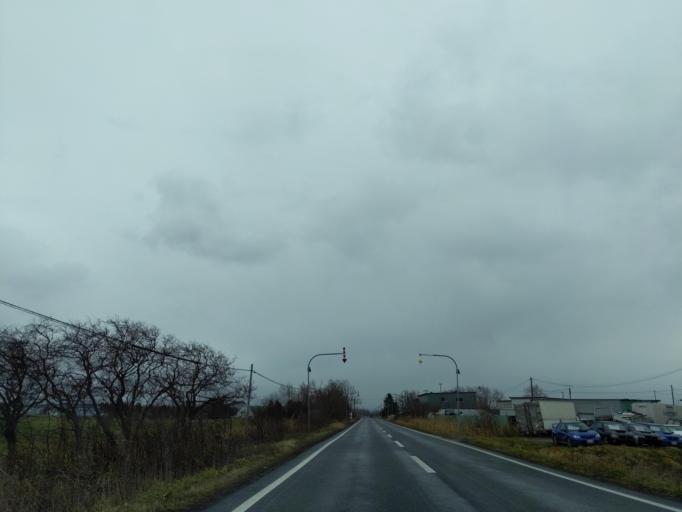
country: JP
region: Hokkaido
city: Ebetsu
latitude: 43.1000
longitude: 141.6119
